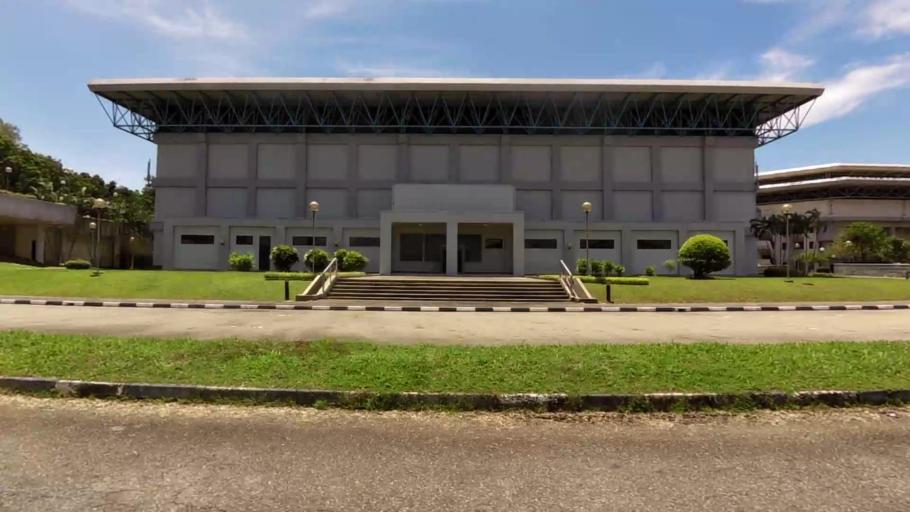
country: BN
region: Brunei and Muara
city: Bandar Seri Begawan
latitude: 4.9287
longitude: 114.9478
